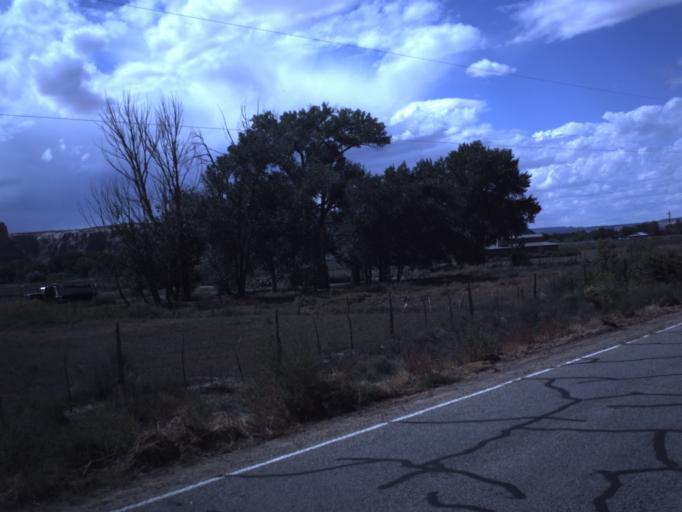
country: US
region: Utah
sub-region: San Juan County
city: Blanding
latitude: 37.2846
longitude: -109.5313
